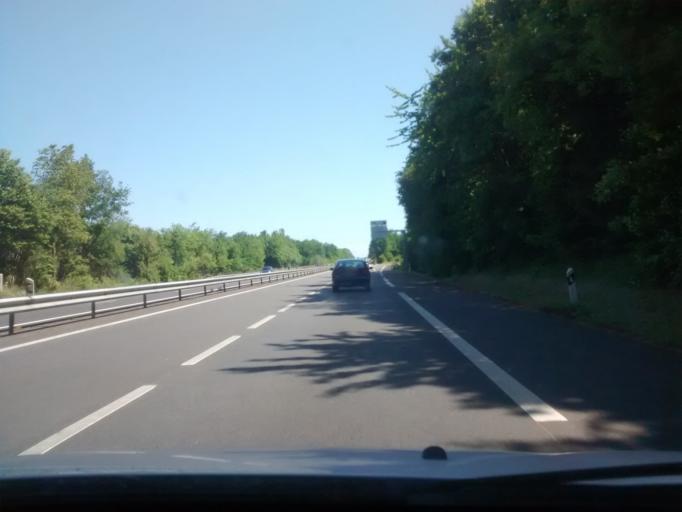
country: FR
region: Brittany
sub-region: Departement d'Ille-et-Vilaine
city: Tinteniac
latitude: 48.3280
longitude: -1.8545
